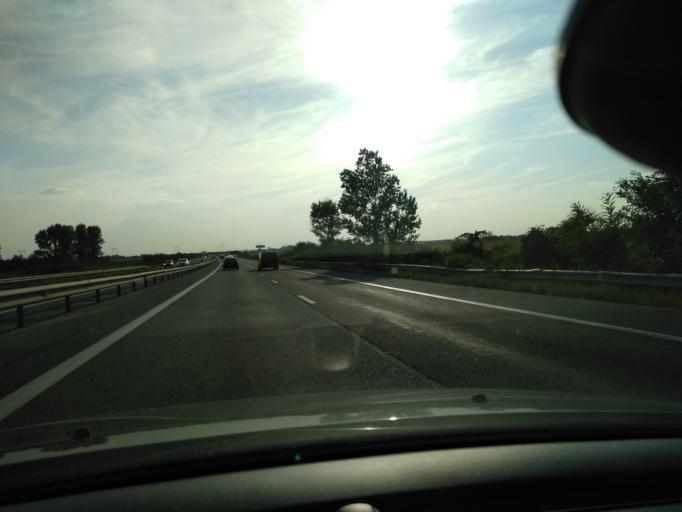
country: RO
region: Giurgiu
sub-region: Comuna Bolintin Vale
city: Bolintin Vale
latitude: 44.4671
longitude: 25.7655
